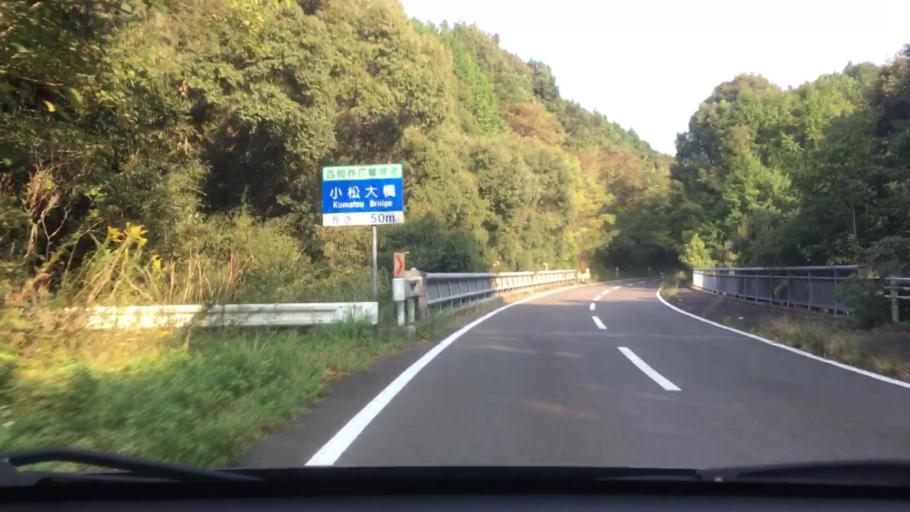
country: JP
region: Nagasaki
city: Sasebo
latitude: 32.9986
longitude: 129.7077
